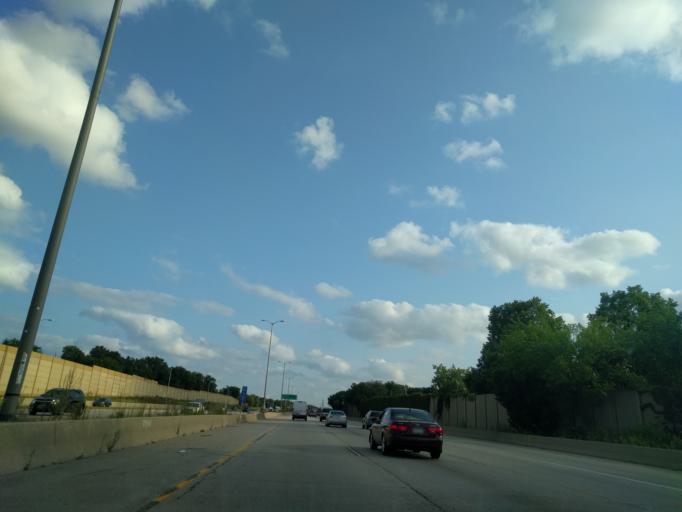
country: US
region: Wisconsin
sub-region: Milwaukee County
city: Saint Francis
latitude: 42.9794
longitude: -87.9164
